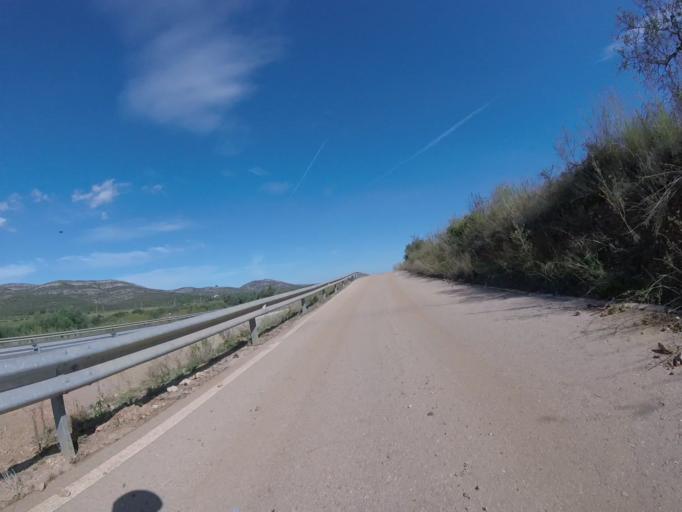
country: ES
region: Valencia
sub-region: Provincia de Castello
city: Santa Magdalena de Pulpis
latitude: 40.3730
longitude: 0.3274
